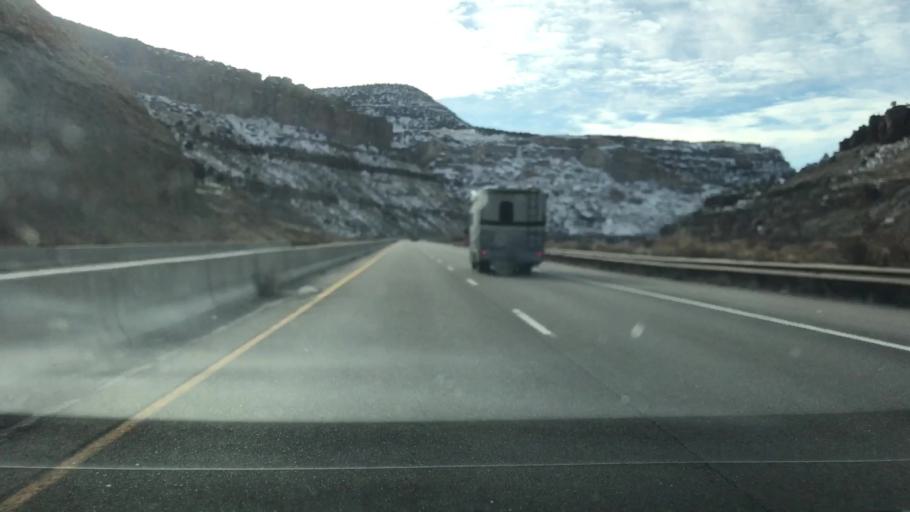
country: US
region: Colorado
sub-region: Mesa County
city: Palisade
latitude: 39.2167
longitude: -108.2565
